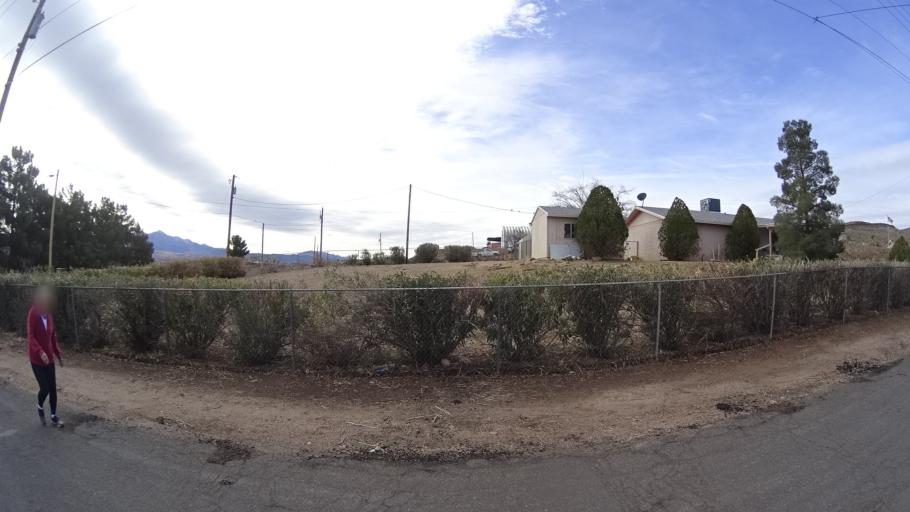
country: US
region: Arizona
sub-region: Mohave County
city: New Kingman-Butler
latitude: 35.2293
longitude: -114.0487
